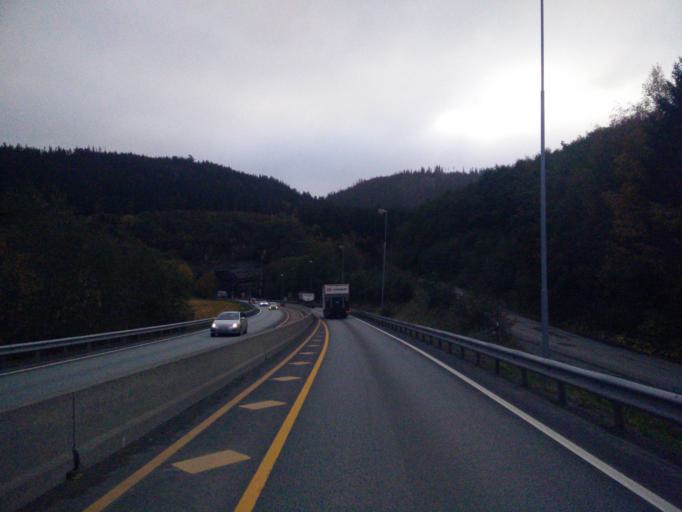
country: NO
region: Sor-Trondelag
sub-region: Malvik
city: Malvik
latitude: 63.4239
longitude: 10.5773
